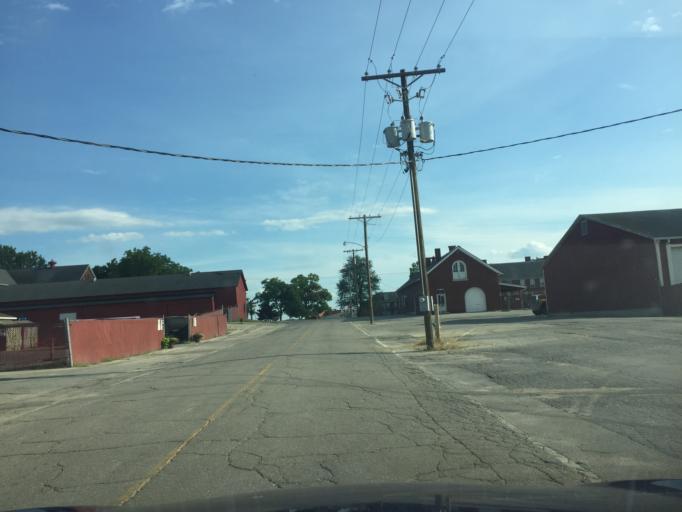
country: US
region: Kansas
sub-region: Leavenworth County
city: Leavenworth
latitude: 39.3576
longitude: -94.9243
